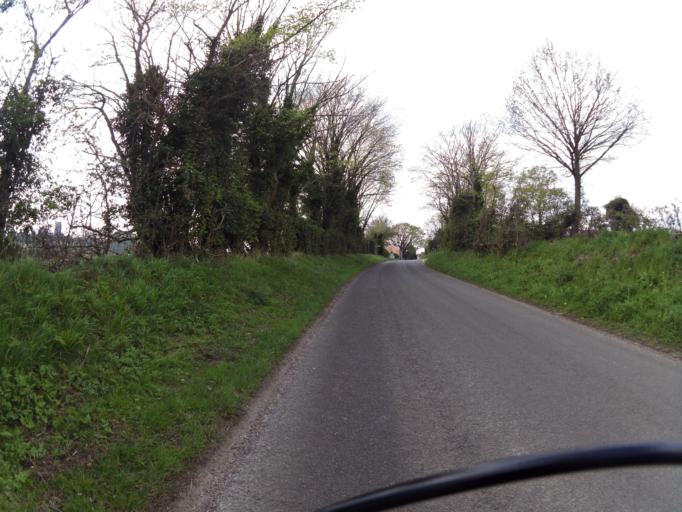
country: GB
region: England
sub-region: Suffolk
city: Hadleigh
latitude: 52.0619
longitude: 0.9195
